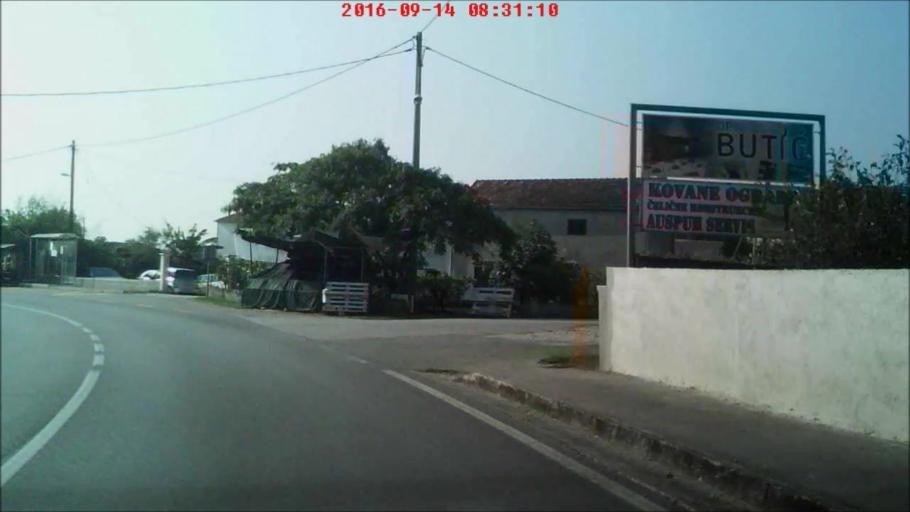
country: HR
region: Zadarska
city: Zadar
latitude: 44.1684
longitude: 15.2949
